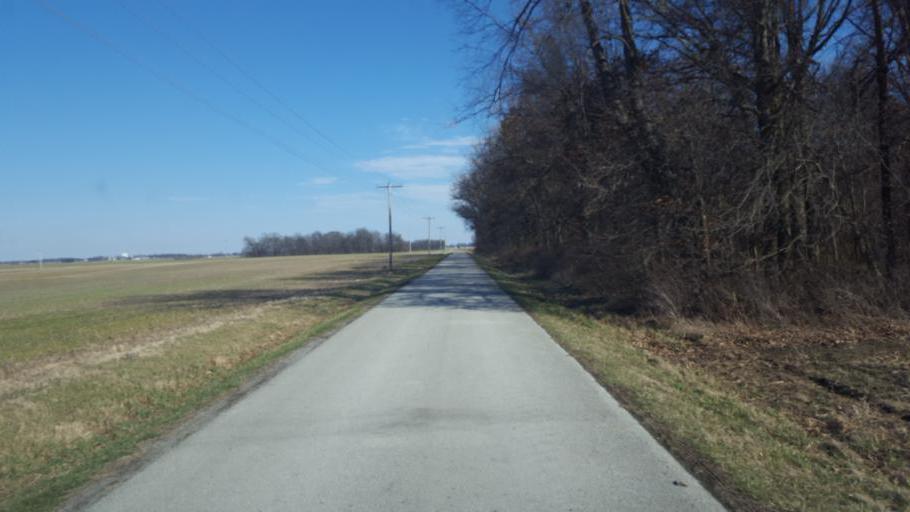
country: US
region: Ohio
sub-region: Marion County
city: Marion
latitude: 40.7022
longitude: -83.2111
